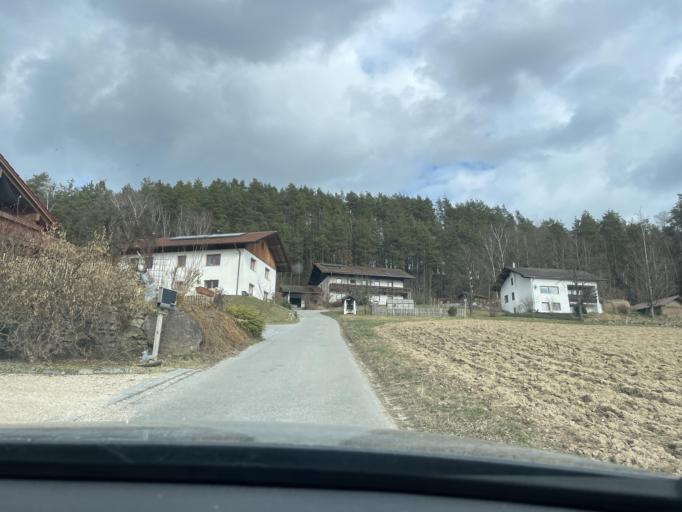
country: DE
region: Bavaria
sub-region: Lower Bavaria
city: Viechtach
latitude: 49.0726
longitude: 12.9109
